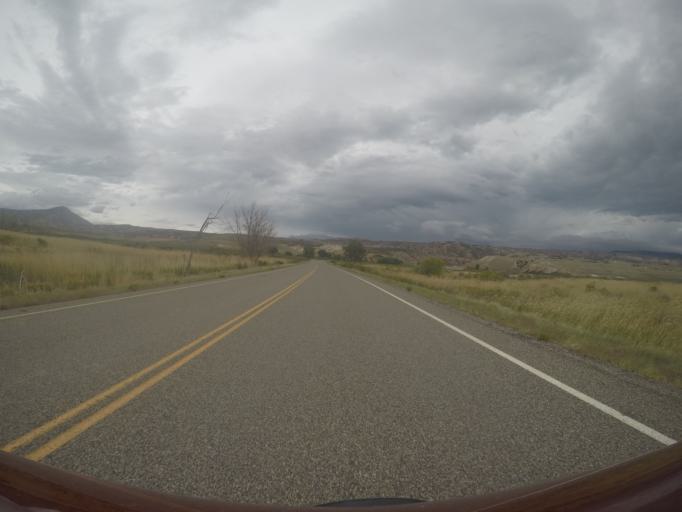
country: US
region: Wyoming
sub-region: Big Horn County
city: Lovell
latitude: 44.9659
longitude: -108.2737
